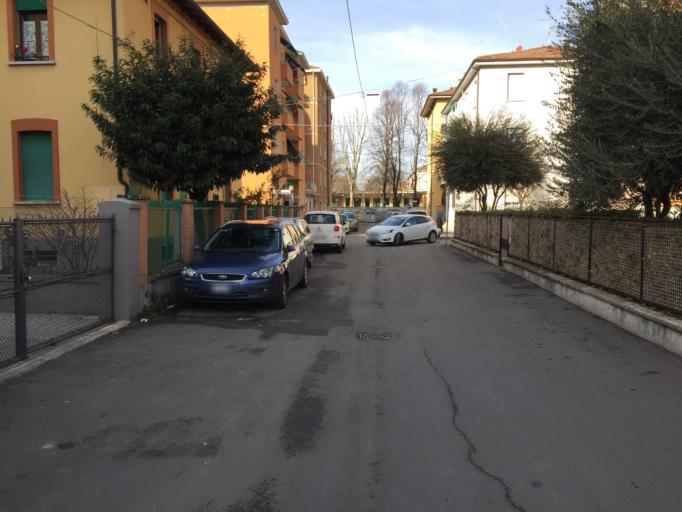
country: IT
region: Emilia-Romagna
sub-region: Provincia di Bologna
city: Calderara di Reno
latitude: 44.5203
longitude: 11.2761
